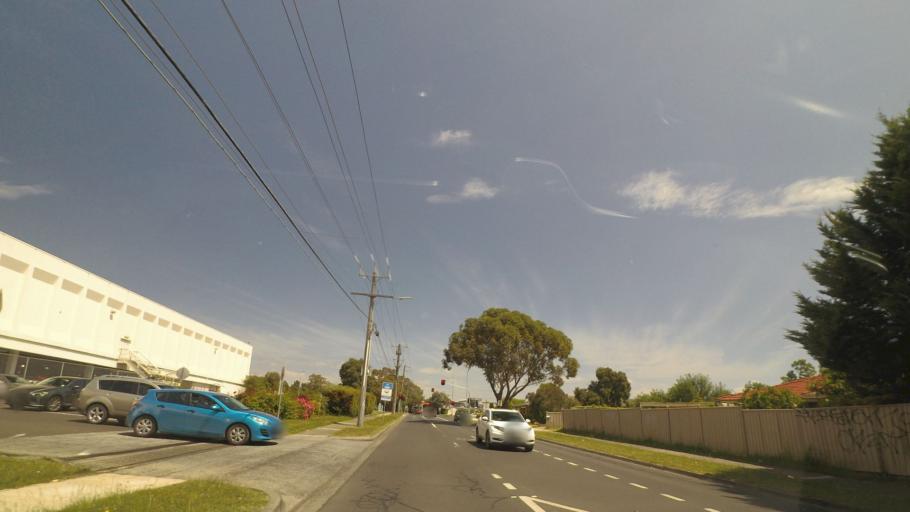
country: AU
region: Victoria
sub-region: Yarra Ranges
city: Chirnside Park
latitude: -37.7568
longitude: 145.3113
